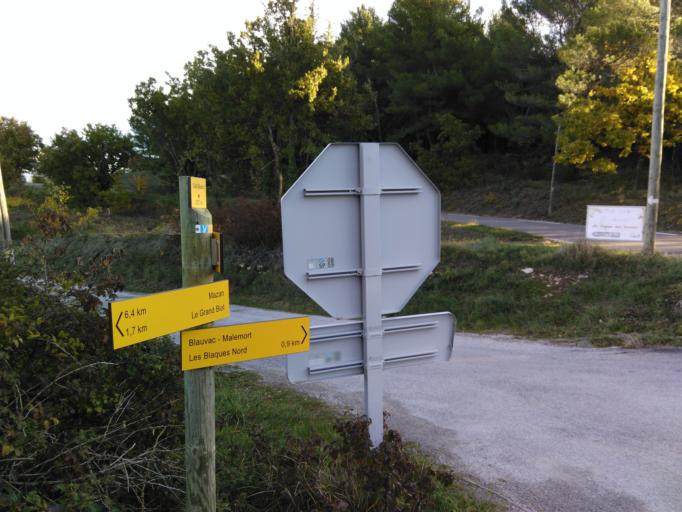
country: FR
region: Provence-Alpes-Cote d'Azur
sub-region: Departement du Vaucluse
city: Malemort-du-Comtat
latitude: 44.0348
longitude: 5.1853
